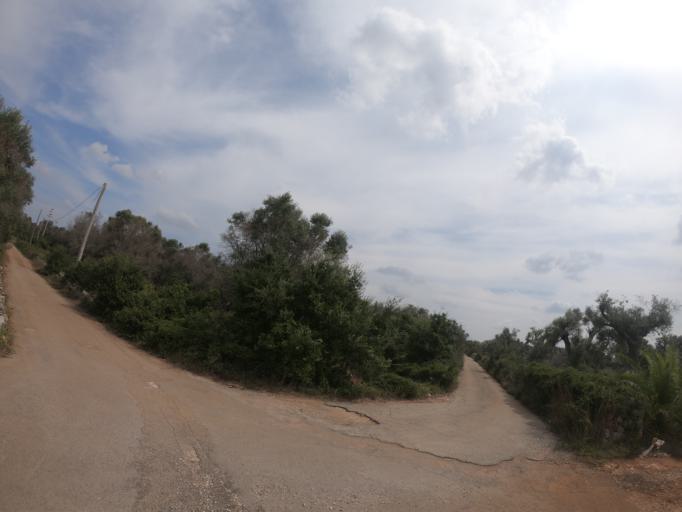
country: IT
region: Apulia
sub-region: Provincia di Lecce
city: Specchia
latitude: 39.9335
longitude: 18.2757
